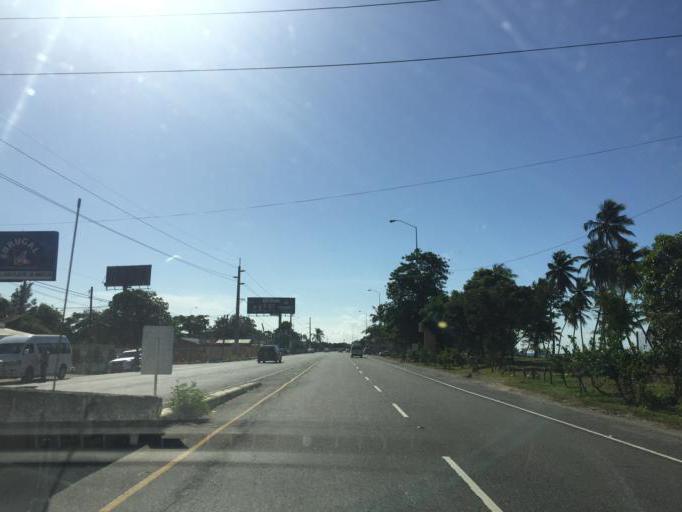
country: DO
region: Santo Domingo
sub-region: Santo Domingo
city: Boca Chica
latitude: 18.4479
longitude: -69.6819
